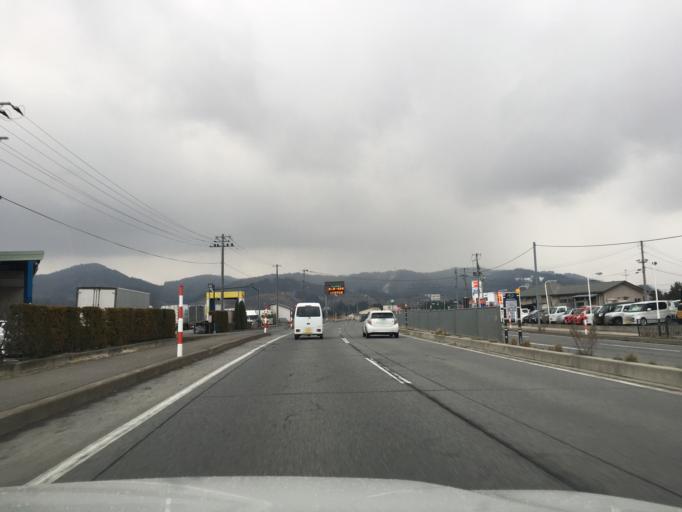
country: JP
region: Aomori
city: Hirosaki
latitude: 40.5539
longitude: 140.5501
